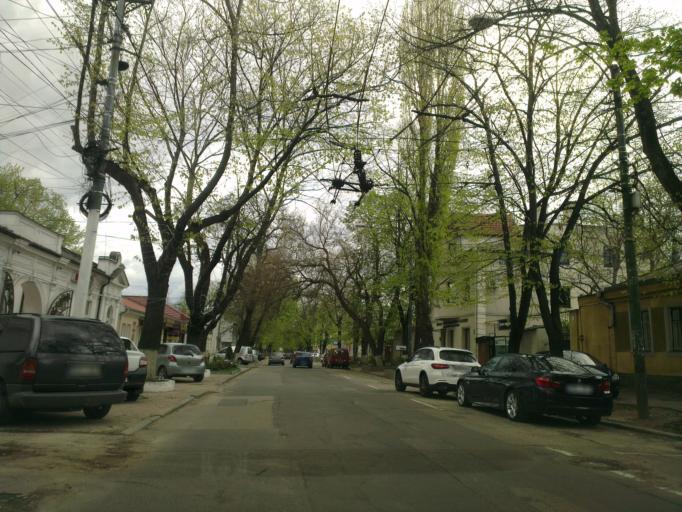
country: MD
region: Chisinau
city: Chisinau
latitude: 47.0145
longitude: 28.8332
